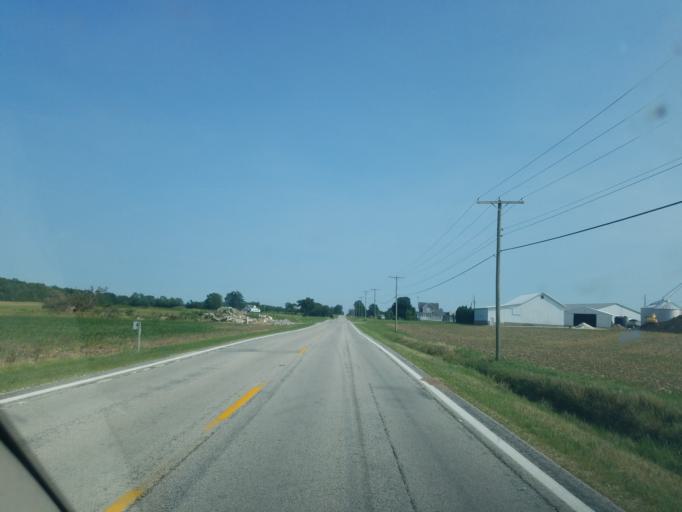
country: US
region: Ohio
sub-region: Wyandot County
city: Carey
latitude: 41.0402
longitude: -83.3083
